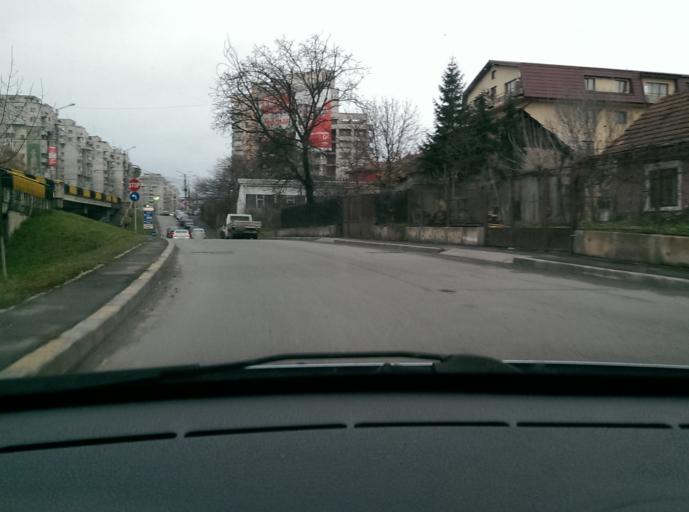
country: RO
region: Cluj
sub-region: Municipiul Cluj-Napoca
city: Cluj-Napoca
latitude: 46.7795
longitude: 23.6198
